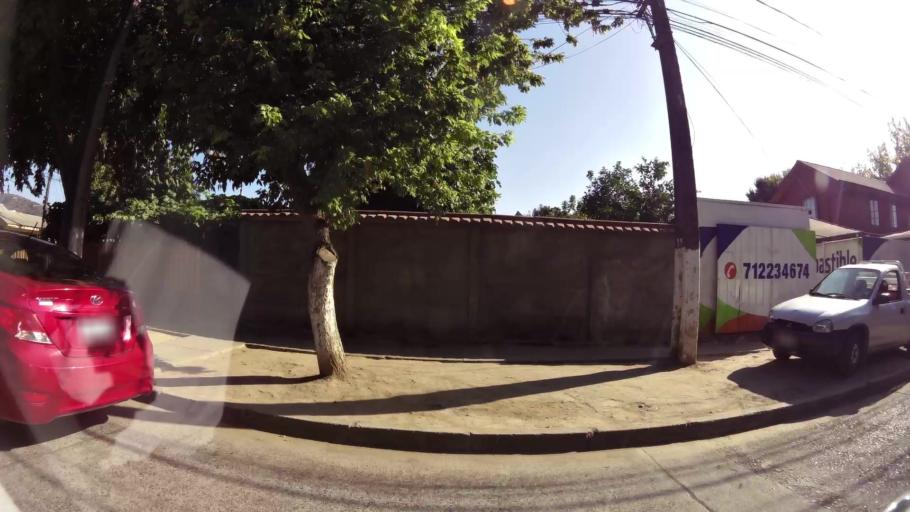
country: CL
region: Maule
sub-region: Provincia de Talca
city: Talca
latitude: -35.4180
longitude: -71.6704
